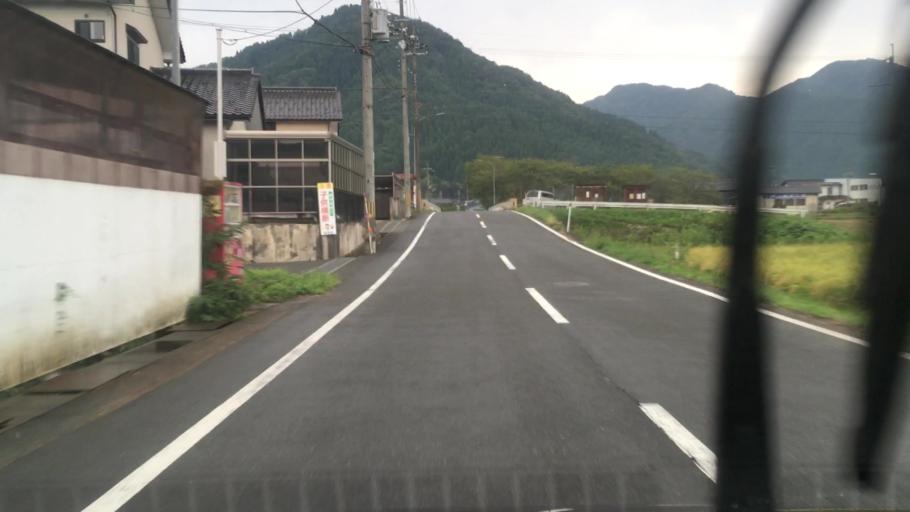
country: JP
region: Hyogo
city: Toyooka
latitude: 35.4574
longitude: 134.7354
